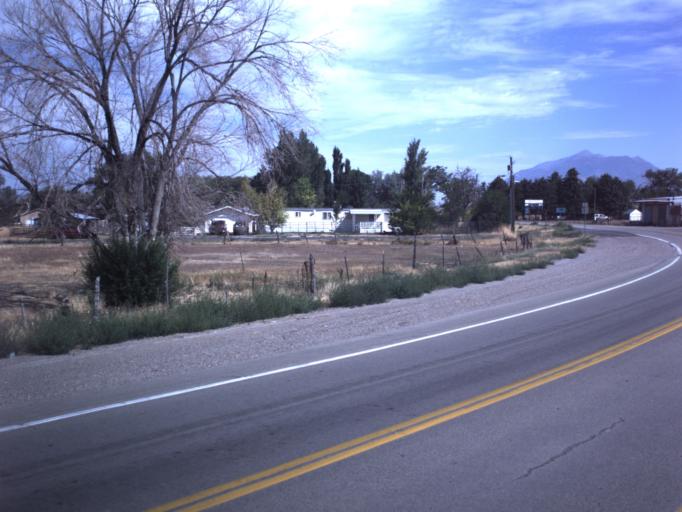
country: US
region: Utah
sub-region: Juab County
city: Nephi
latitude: 39.5595
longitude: -111.8624
